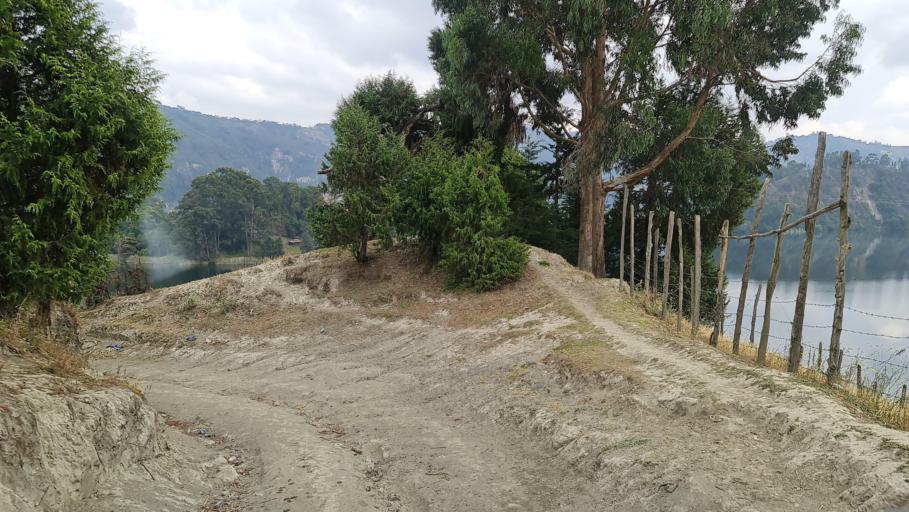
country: ET
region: Oromiya
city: Hagere Hiywet
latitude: 8.7997
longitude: 37.8921
